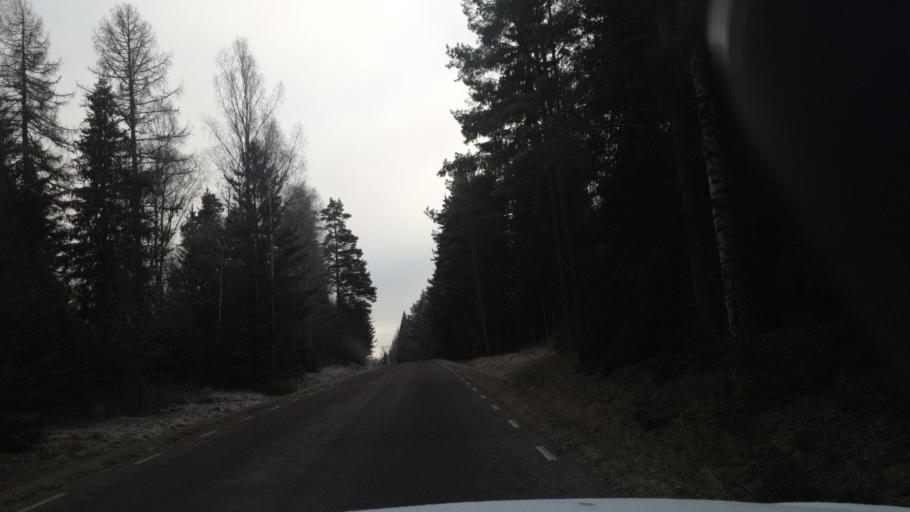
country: SE
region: Vaermland
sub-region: Karlstads Kommun
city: Valberg
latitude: 59.4615
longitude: 13.0834
